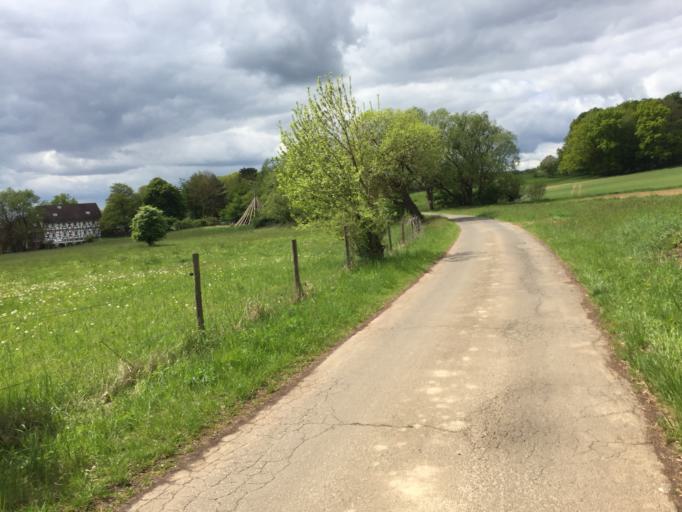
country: DE
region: Hesse
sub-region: Regierungsbezirk Giessen
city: Grunberg
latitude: 50.5726
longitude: 8.9095
